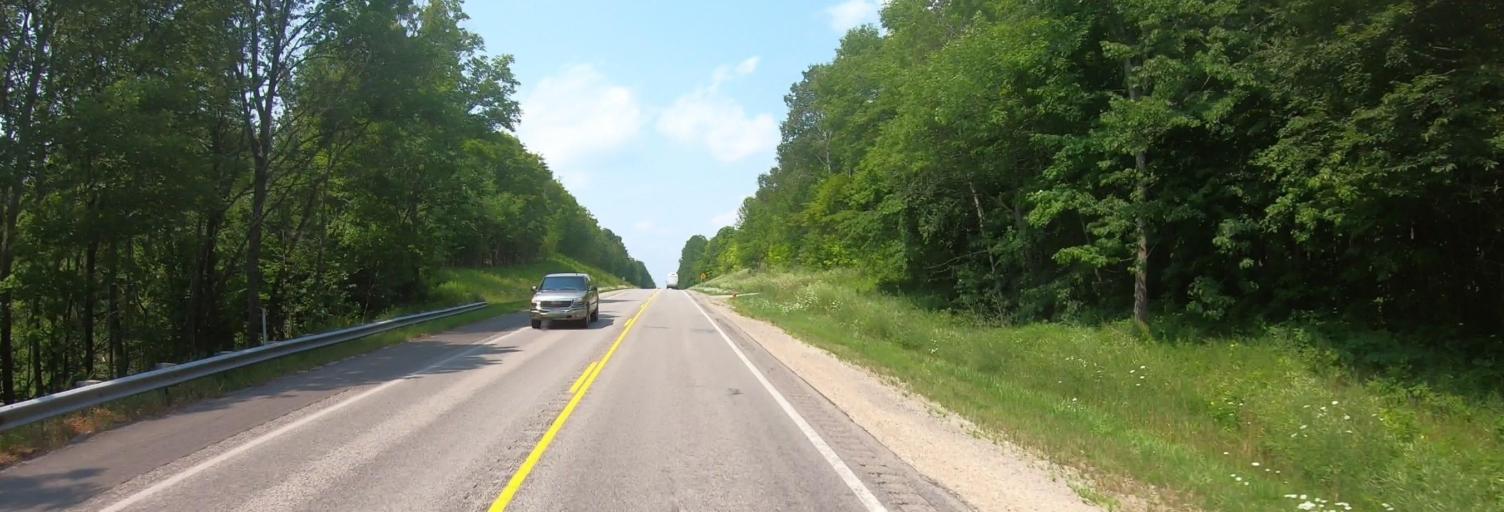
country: US
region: Michigan
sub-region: Luce County
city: Newberry
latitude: 46.3356
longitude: -85.8015
